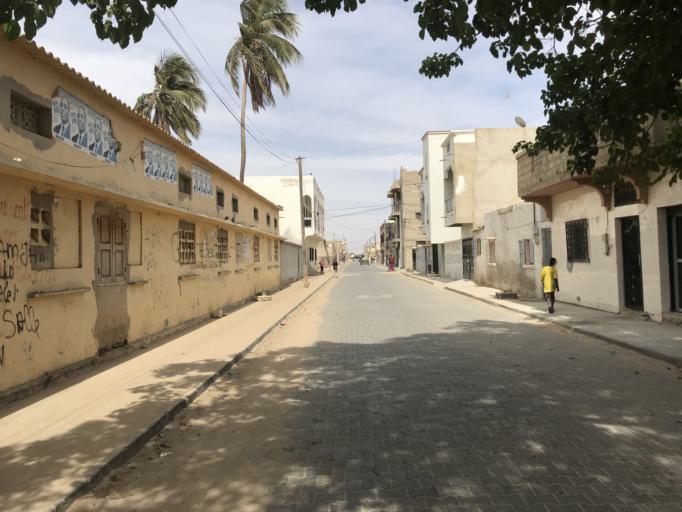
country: SN
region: Saint-Louis
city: Saint-Louis
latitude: 16.0228
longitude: -16.4860
